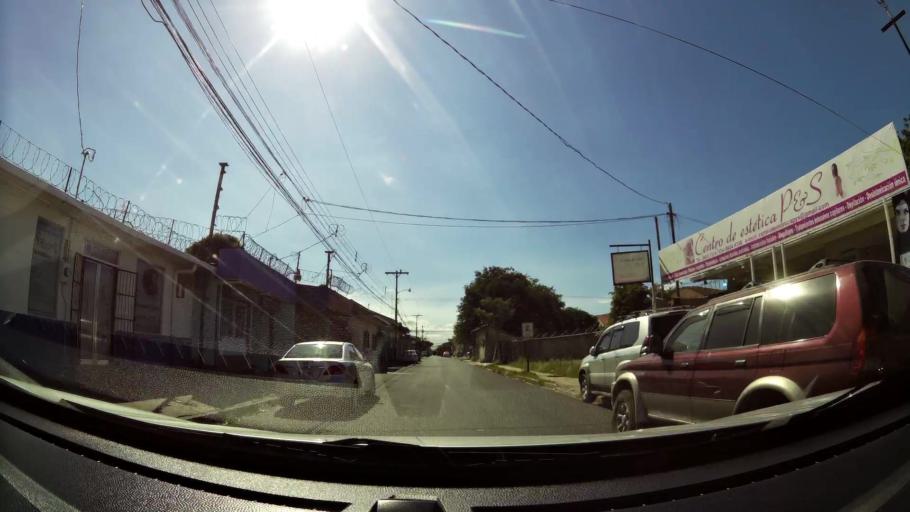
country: CR
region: Guanacaste
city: Liberia
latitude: 10.6319
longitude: -85.4343
